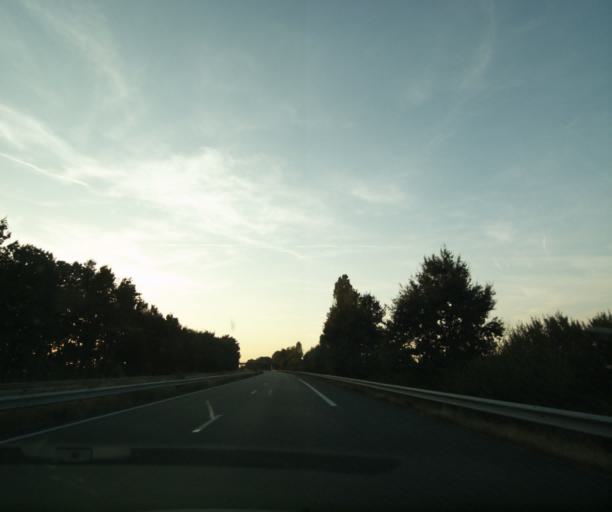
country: FR
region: Aquitaine
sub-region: Departement du Lot-et-Garonne
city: Fourques-sur-Garonne
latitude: 44.4242
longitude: 0.1646
